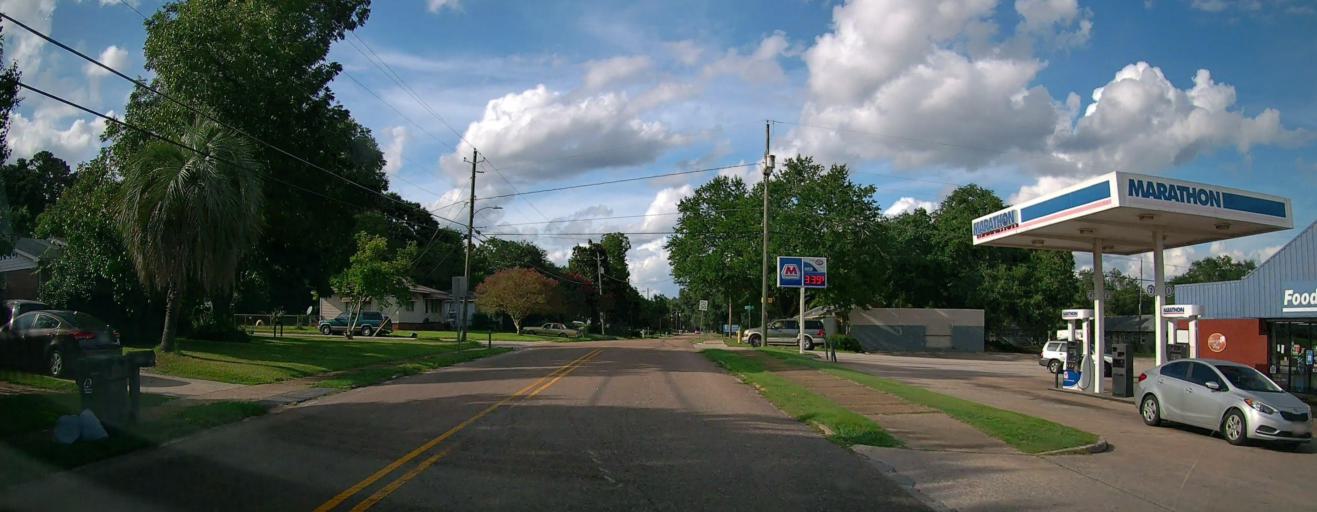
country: US
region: Alabama
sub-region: Russell County
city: Phenix City
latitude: 32.4825
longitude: -84.9987
